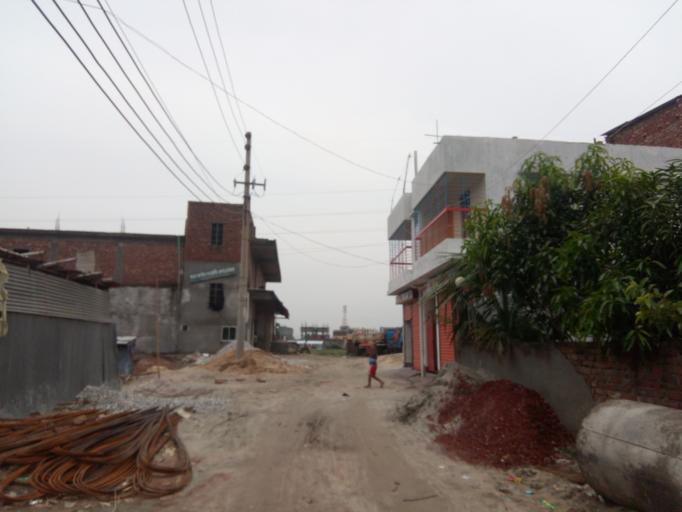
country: BD
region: Dhaka
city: Azimpur
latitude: 23.7441
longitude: 90.3522
